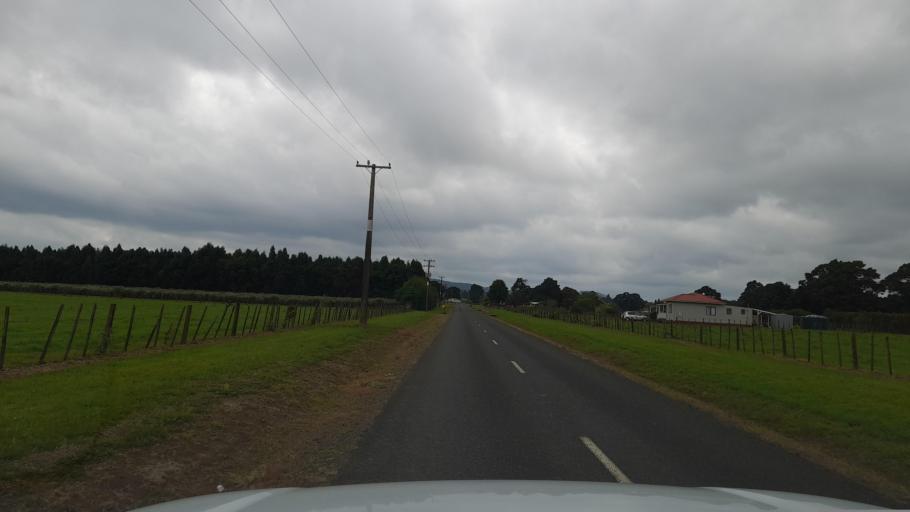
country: NZ
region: Northland
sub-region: Far North District
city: Waimate North
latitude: -35.4276
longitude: 173.7937
